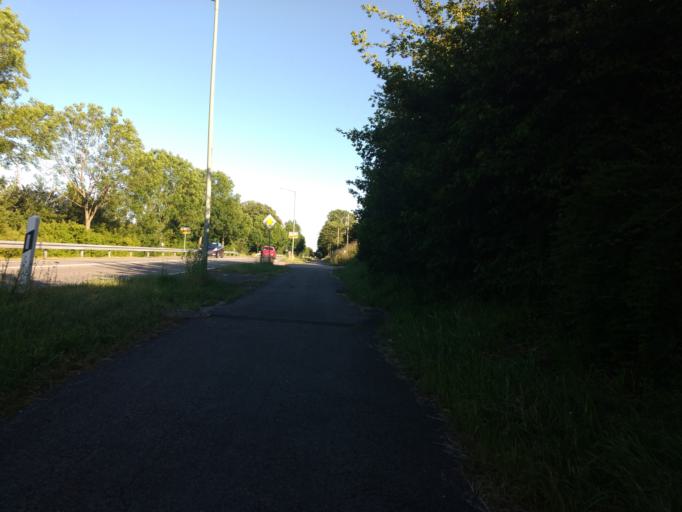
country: DE
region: Saarland
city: Rehlingen-Siersburg
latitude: 49.3998
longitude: 6.6561
